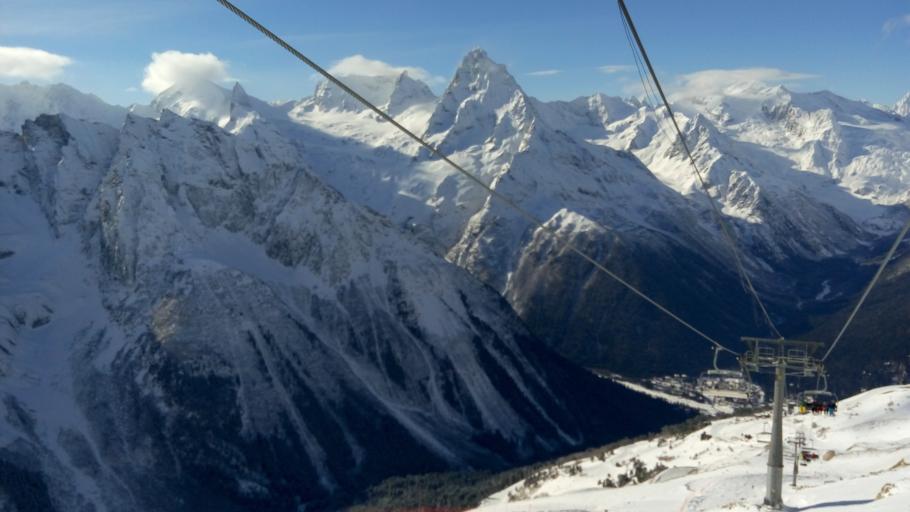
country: RU
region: Karachayevo-Cherkesiya
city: Teberda
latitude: 43.2912
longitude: 41.6684
